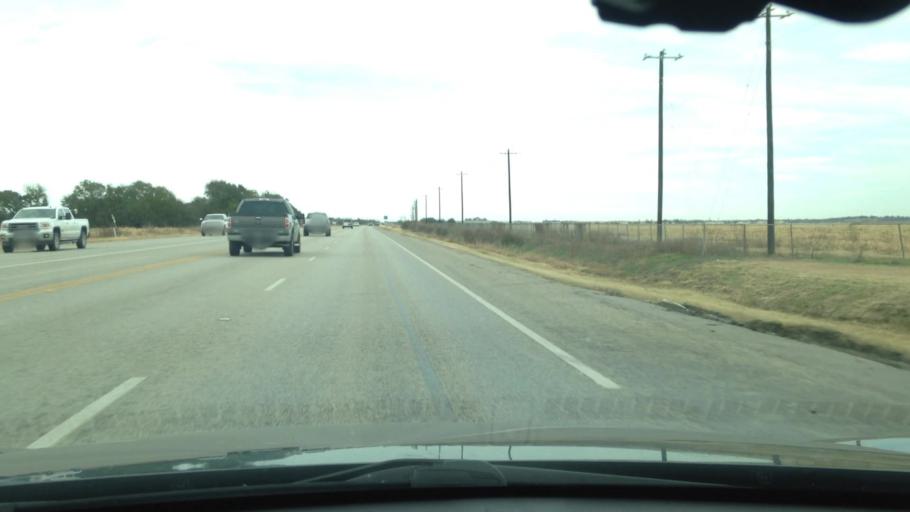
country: US
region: Texas
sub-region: Caldwell County
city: Martindale
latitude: 29.8945
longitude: -97.8795
